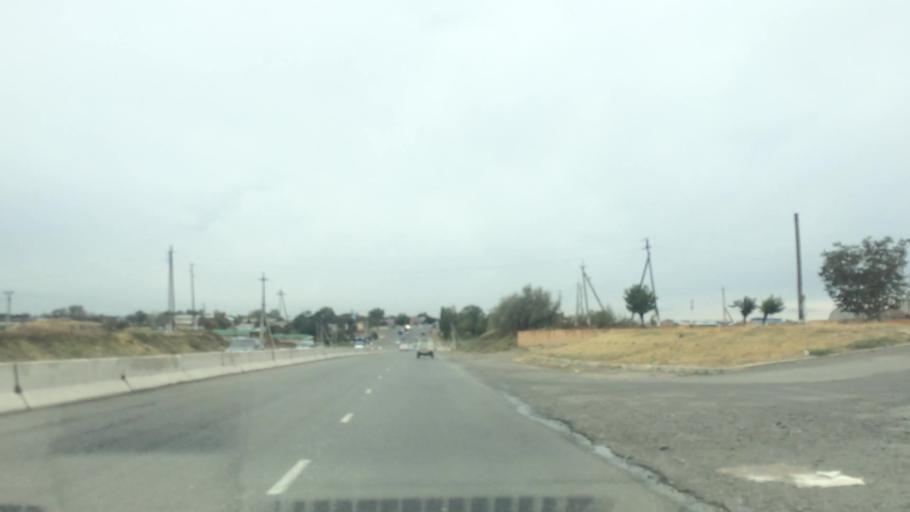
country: UZ
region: Samarqand
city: Bulung'ur
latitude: 39.7744
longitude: 67.2826
